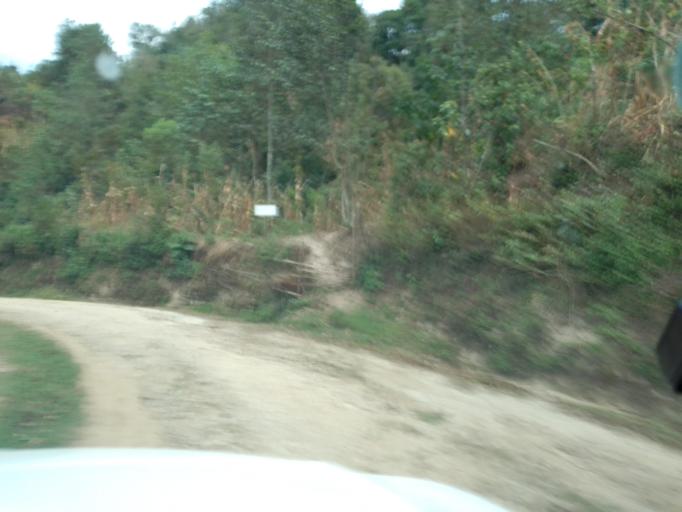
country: MX
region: Chiapas
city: Motozintla de Mendoza
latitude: 15.2161
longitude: -92.2295
